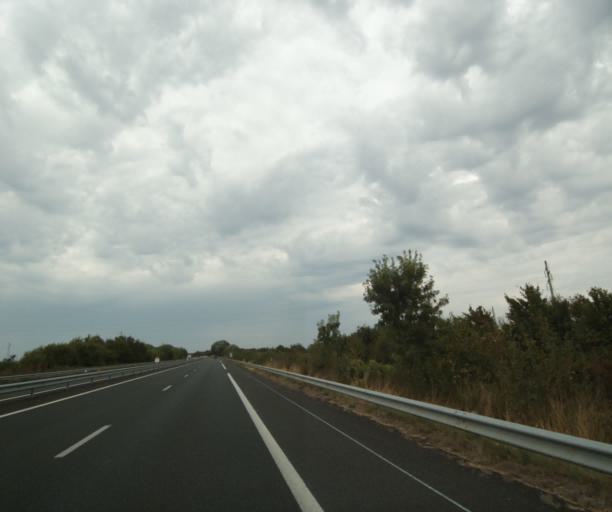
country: FR
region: Poitou-Charentes
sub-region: Departement de la Charente-Maritime
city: Tonnay-Charente
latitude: 45.9558
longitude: -0.9072
